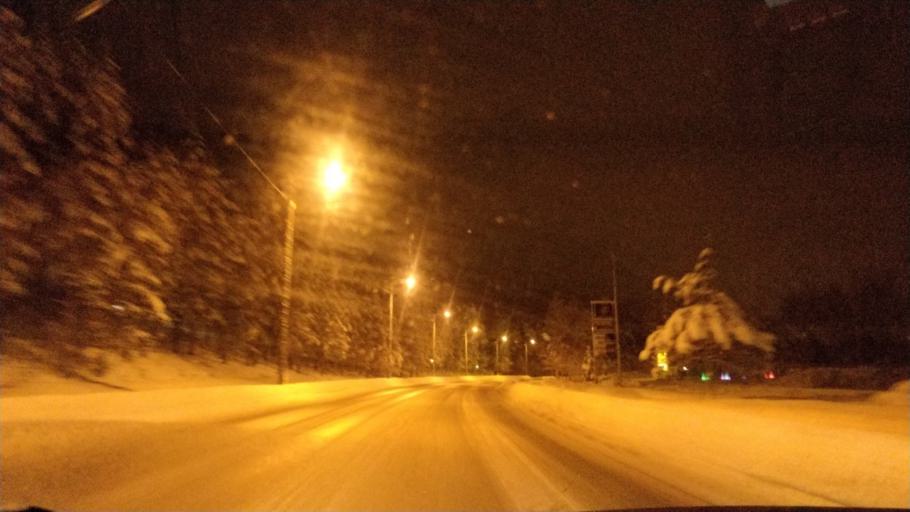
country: FI
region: Lapland
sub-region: Rovaniemi
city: Rovaniemi
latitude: 66.3759
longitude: 25.3833
